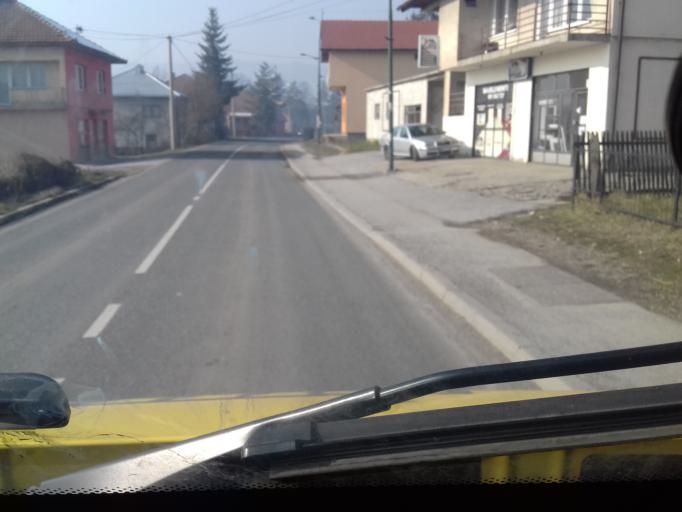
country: BA
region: Federation of Bosnia and Herzegovina
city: Ilijas
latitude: 43.9515
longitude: 18.2681
